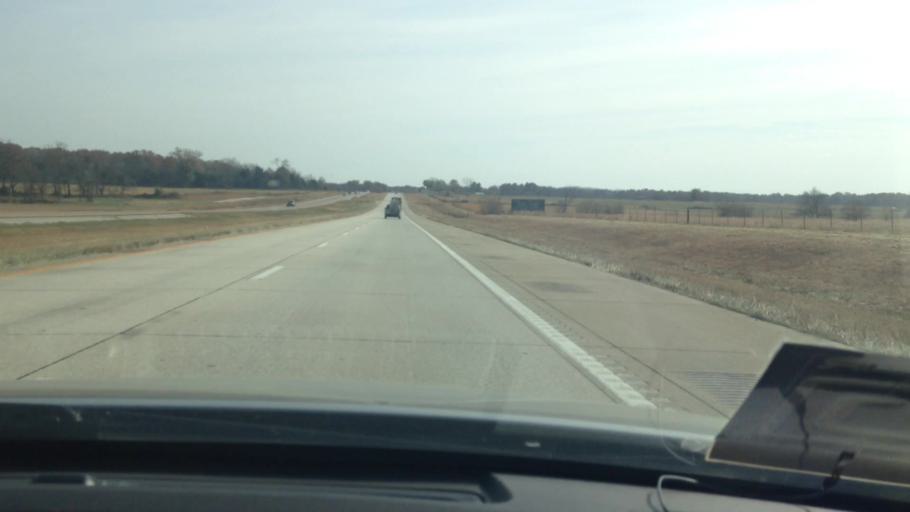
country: US
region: Missouri
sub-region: Henry County
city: Clinton
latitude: 38.4086
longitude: -93.8495
